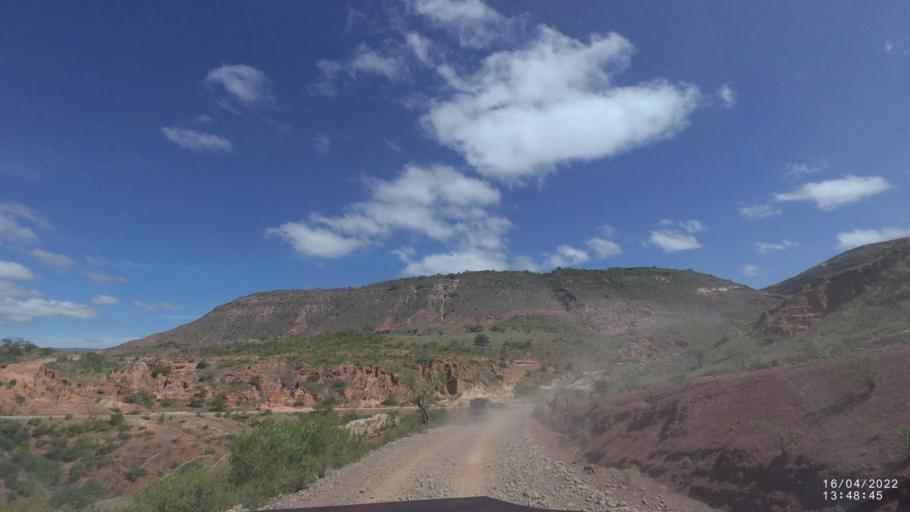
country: BO
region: Cochabamba
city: Mizque
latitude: -18.0123
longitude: -65.5790
